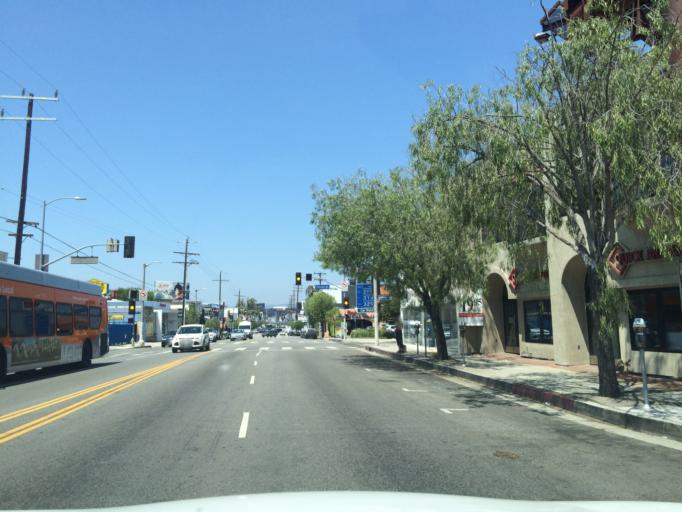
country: US
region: California
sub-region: Los Angeles County
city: West Hollywood
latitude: 34.0717
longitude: -118.3632
